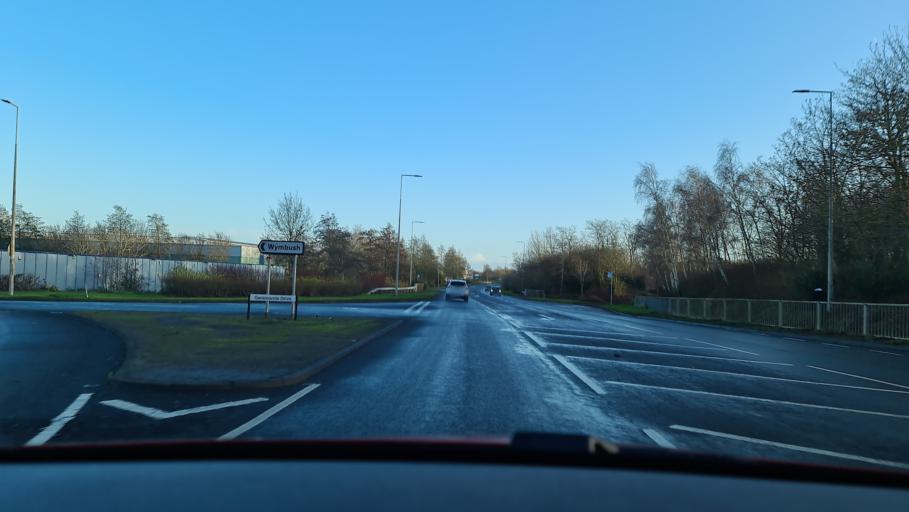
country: GB
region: England
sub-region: Milton Keynes
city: Bradwell
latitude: 52.0439
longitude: -0.8024
